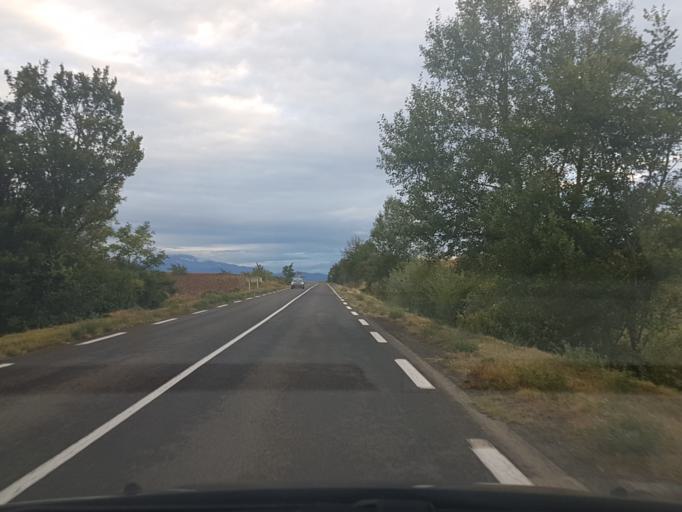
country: FR
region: Midi-Pyrenees
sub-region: Departement de l'Ariege
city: Mirepoix
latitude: 43.1268
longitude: 1.9405
